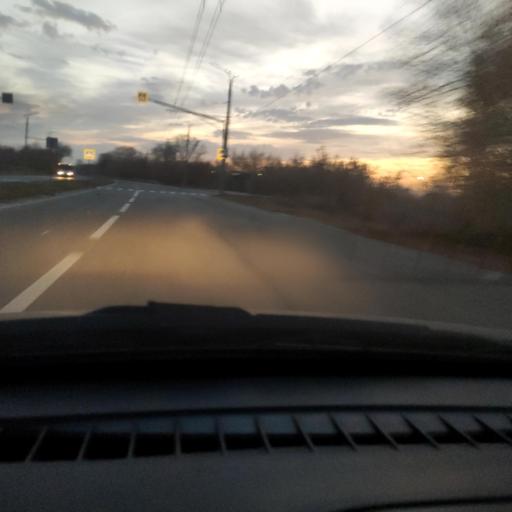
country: RU
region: Samara
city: Zhigulevsk
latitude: 53.5400
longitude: 49.5682
